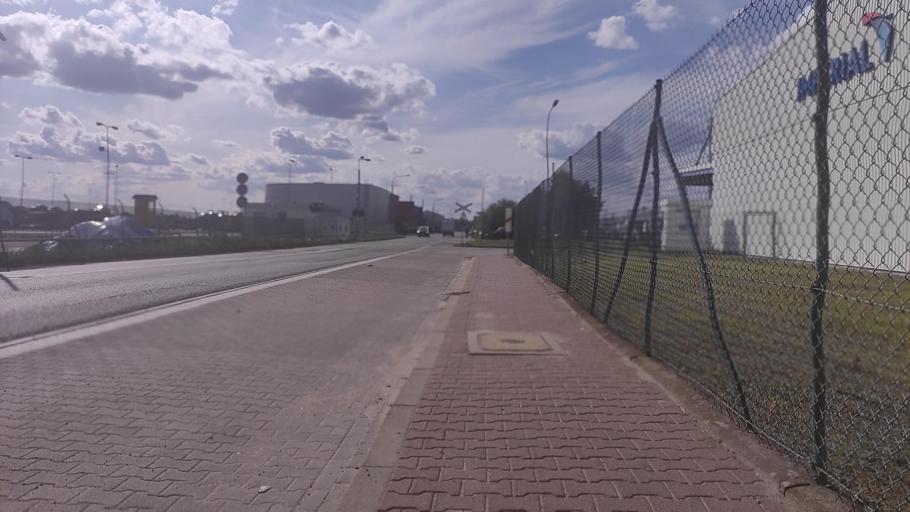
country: PL
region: Greater Poland Voivodeship
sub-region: Powiat poznanski
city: Swarzedz
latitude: 52.3997
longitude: 17.0980
